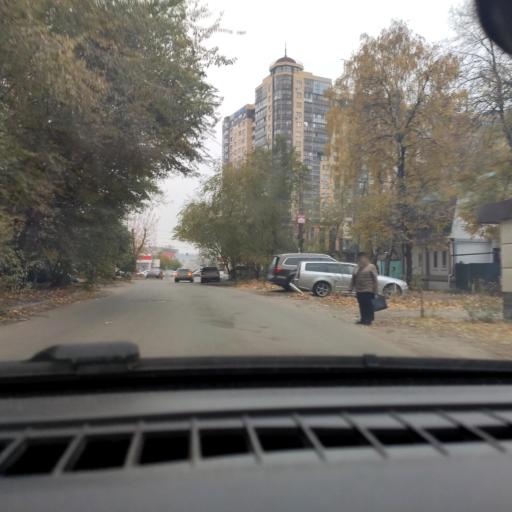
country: RU
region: Voronezj
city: Voronezh
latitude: 51.6717
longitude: 39.1649
